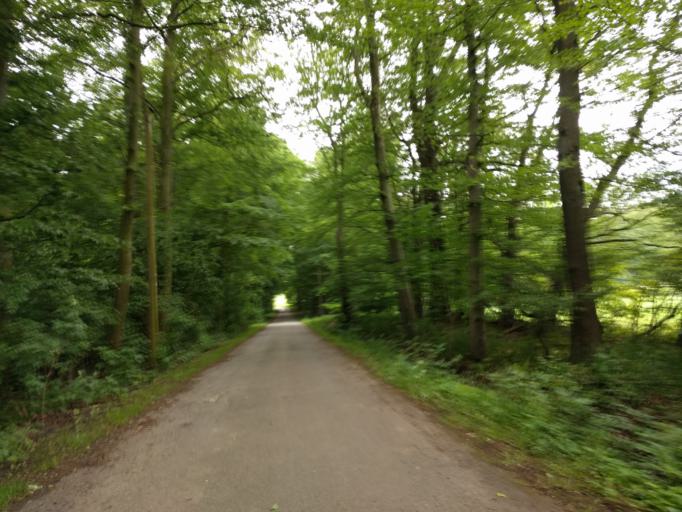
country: DE
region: North Rhine-Westphalia
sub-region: Regierungsbezirk Detmold
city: Bielefeld
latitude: 52.0464
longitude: 8.5676
